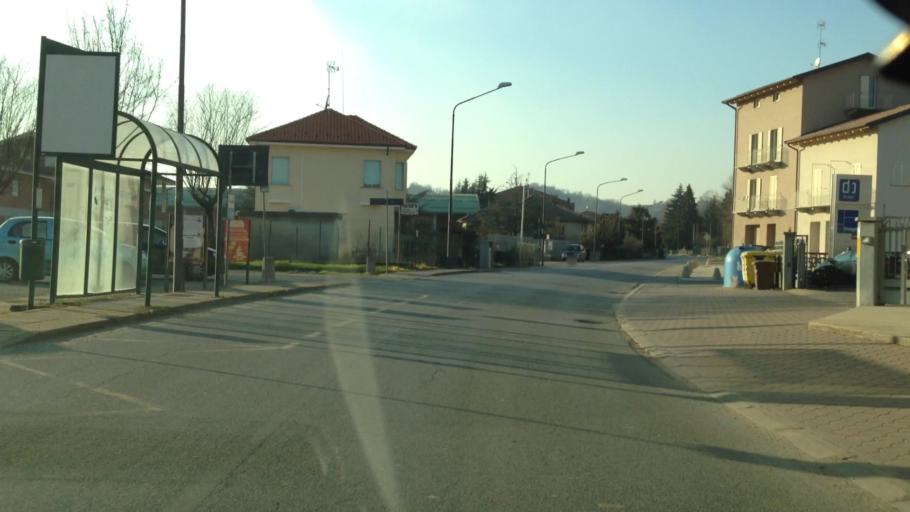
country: IT
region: Piedmont
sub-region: Provincia di Asti
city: Mombercelli
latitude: 44.8229
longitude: 8.2929
